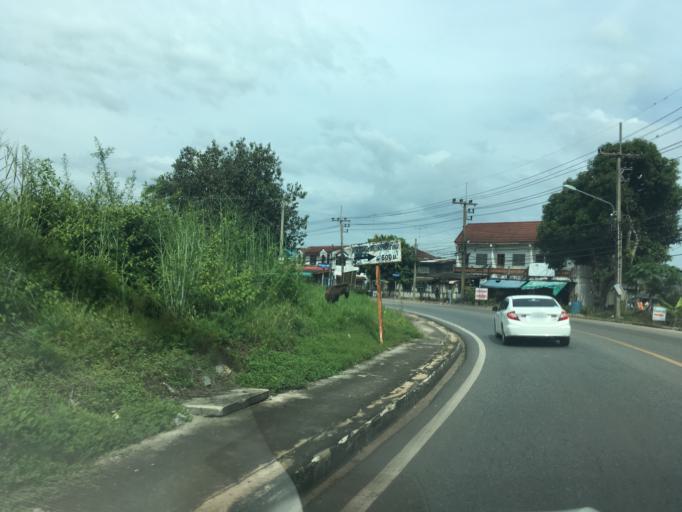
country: TH
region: Chachoengsao
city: Bang Khla
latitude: 13.7410
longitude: 101.2142
